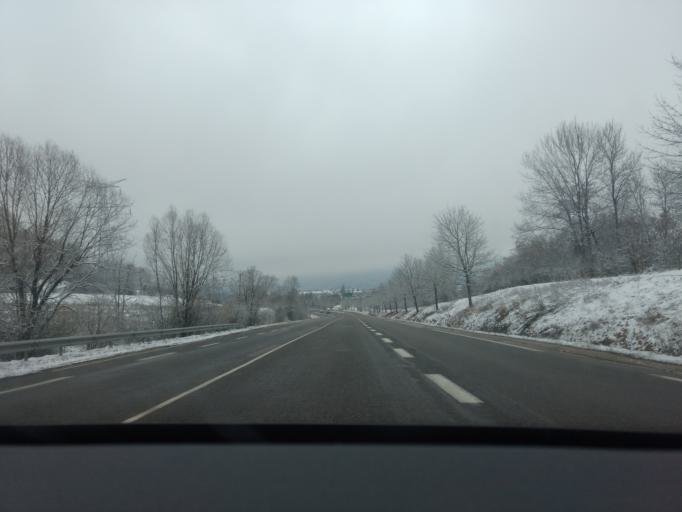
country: FR
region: Franche-Comte
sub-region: Departement du Jura
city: Champagnole
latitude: 46.7647
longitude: 5.9053
